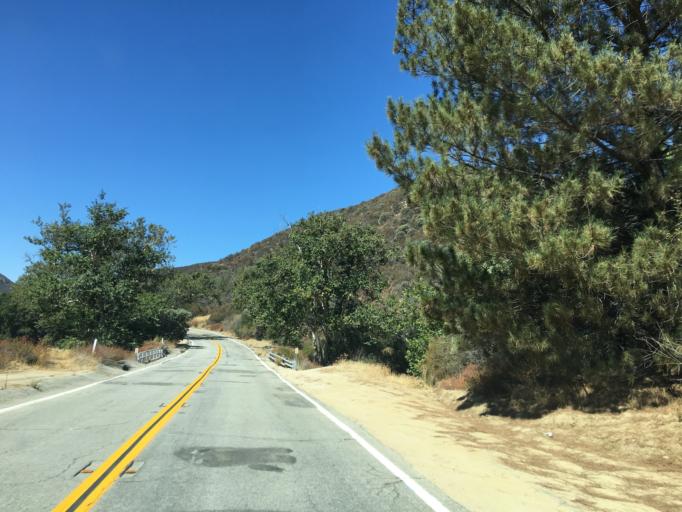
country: US
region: California
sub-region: Los Angeles County
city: Green Valley
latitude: 34.6428
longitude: -118.5218
